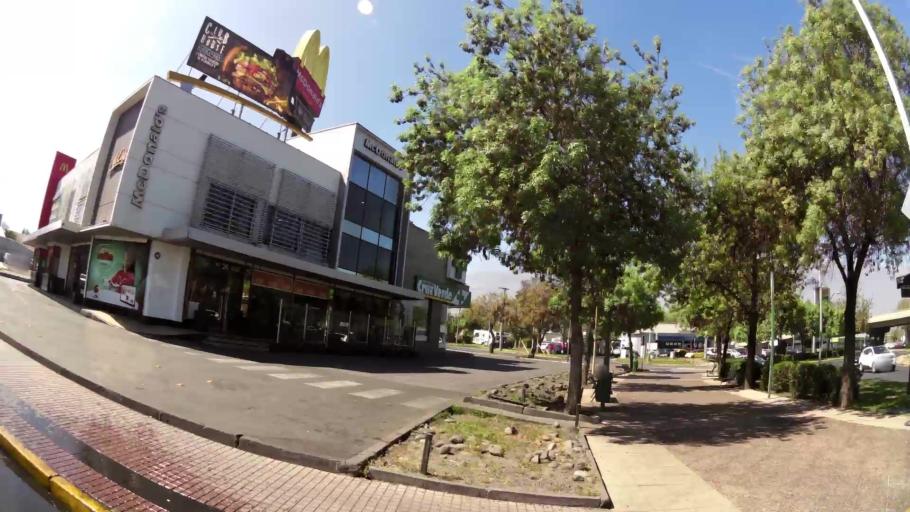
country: CL
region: Santiago Metropolitan
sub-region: Provincia de Santiago
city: Villa Presidente Frei, Nunoa, Santiago, Chile
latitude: -33.4175
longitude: -70.5531
